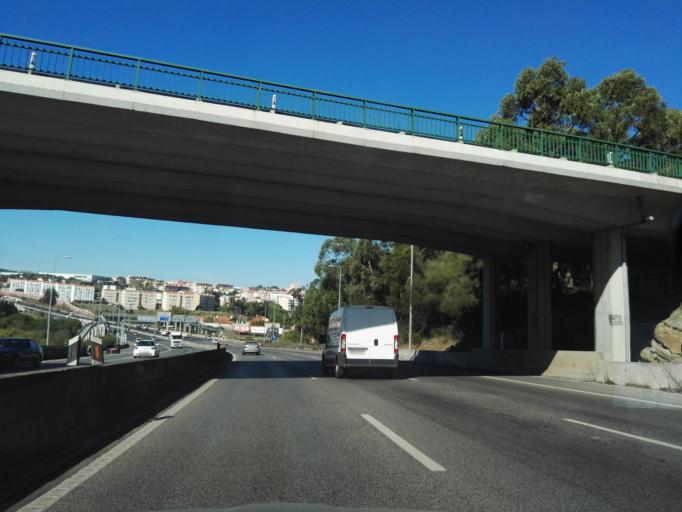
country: PT
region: Lisbon
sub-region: Sintra
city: Rio de Mouro
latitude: 38.7769
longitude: -9.3229
